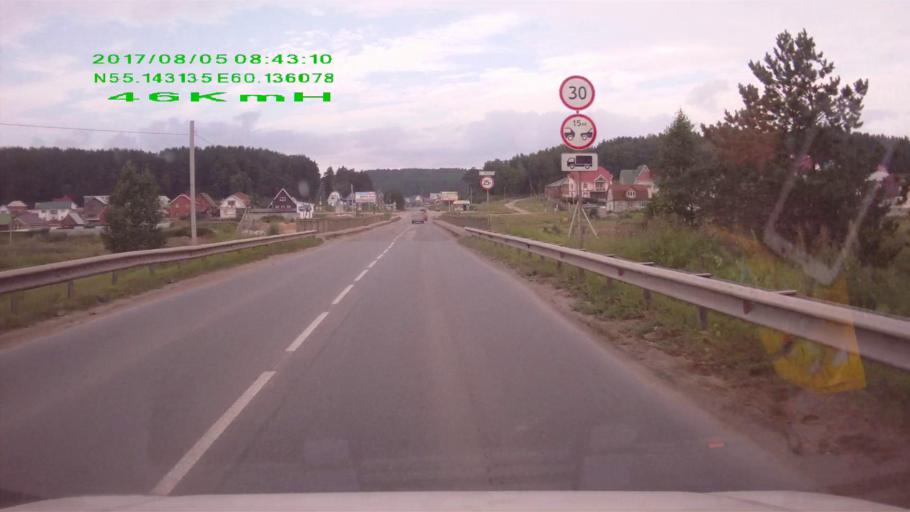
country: RU
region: Chelyabinsk
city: Turgoyak
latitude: 55.1432
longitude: 60.1357
